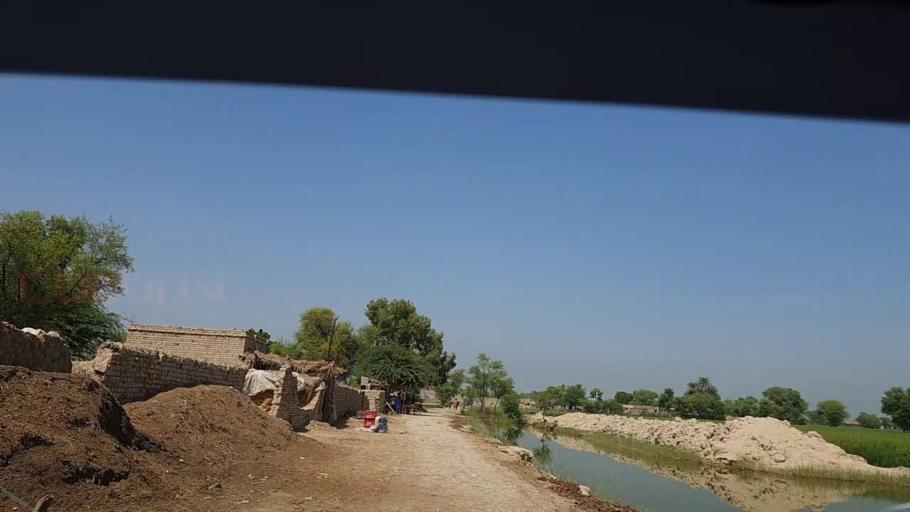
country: PK
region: Sindh
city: Tangwani
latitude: 28.2832
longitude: 69.0375
